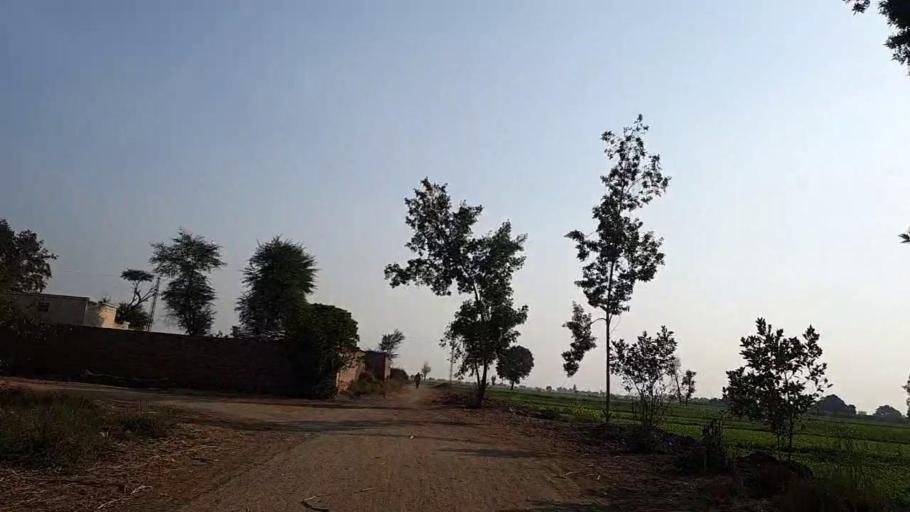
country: PK
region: Sindh
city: Nawabshah
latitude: 26.1396
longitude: 68.3869
